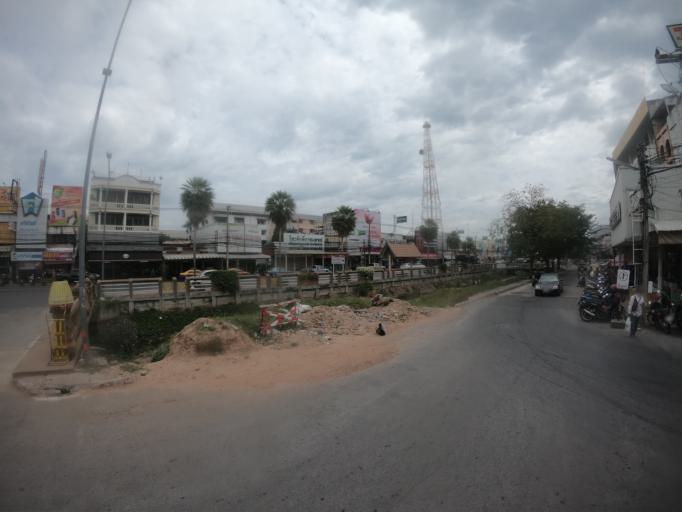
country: TH
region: Maha Sarakham
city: Maha Sarakham
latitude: 16.1812
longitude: 103.3016
